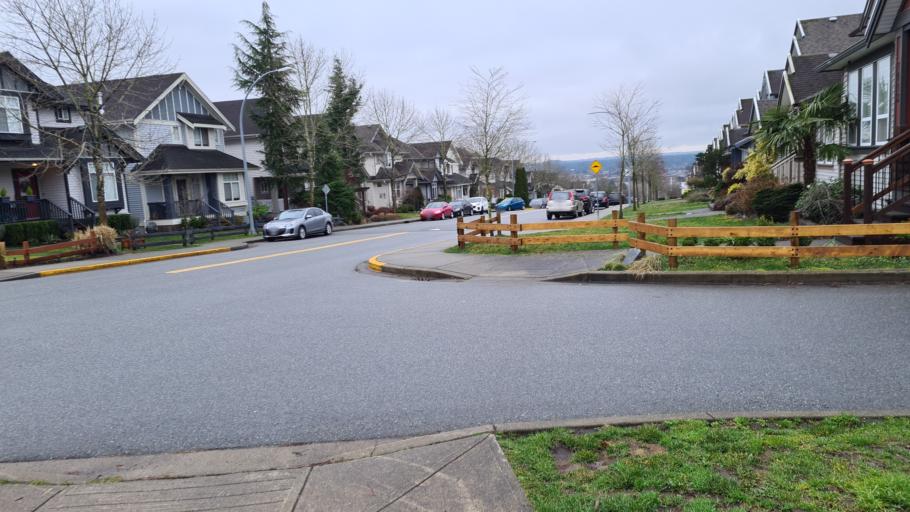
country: CA
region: British Columbia
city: Langley
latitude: 49.1300
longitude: -122.6648
